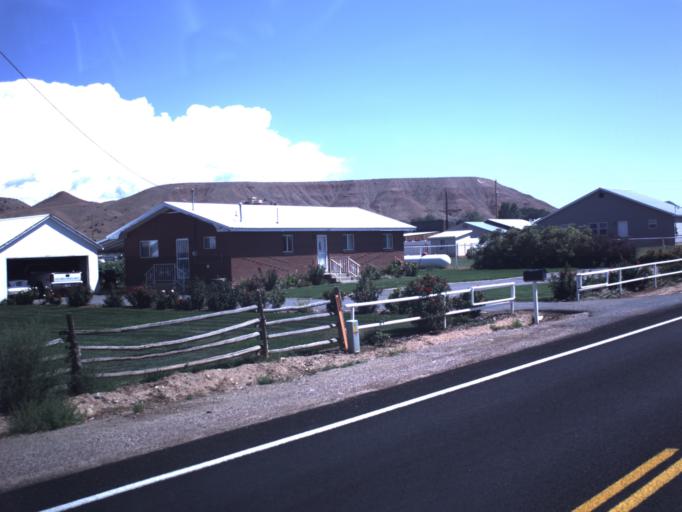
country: US
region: Utah
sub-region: Duchesne County
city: Roosevelt
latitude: 40.4037
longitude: -109.8043
